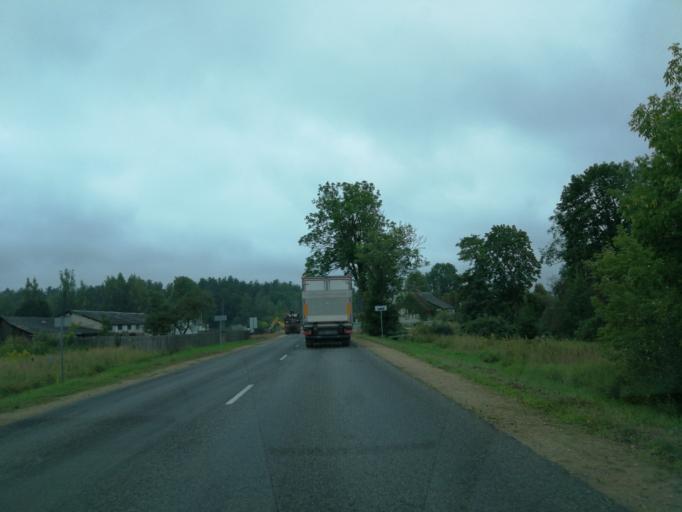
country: LV
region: Livani
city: Livani
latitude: 56.3574
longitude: 26.1871
